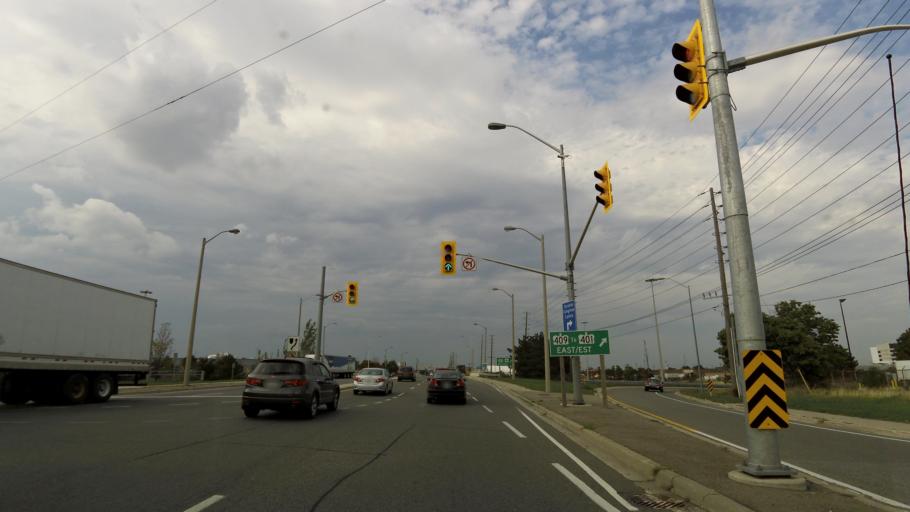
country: CA
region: Ontario
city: Etobicoke
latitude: 43.6978
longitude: -79.5736
